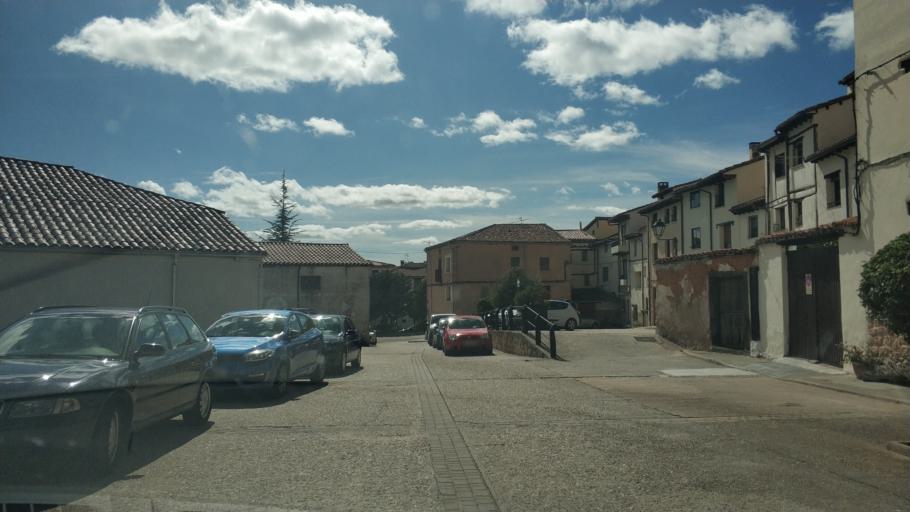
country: ES
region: Castille and Leon
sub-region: Provincia de Burgos
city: Covarrubias
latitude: 42.0607
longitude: -3.5194
